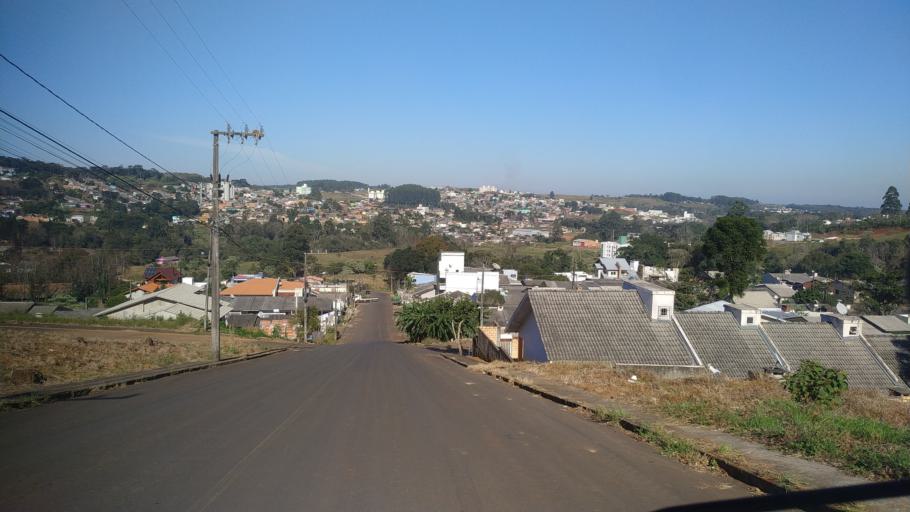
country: BR
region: Santa Catarina
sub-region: Chapeco
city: Chapeco
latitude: -27.1222
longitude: -52.5938
